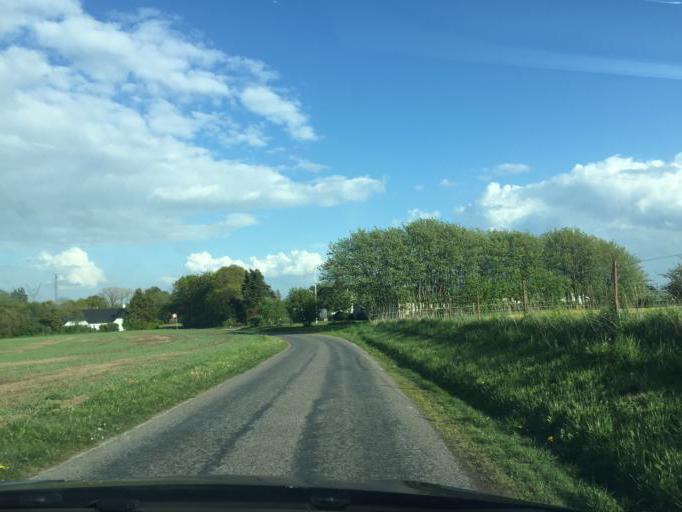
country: DK
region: South Denmark
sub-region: Odense Kommune
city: Bellinge
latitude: 55.3628
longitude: 10.2903
